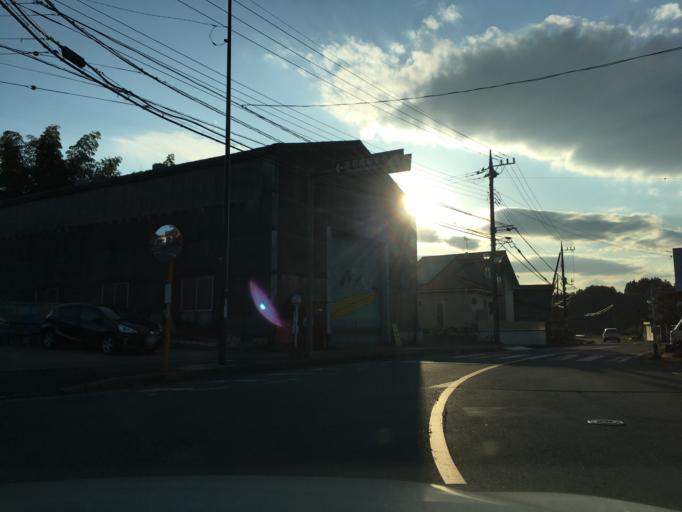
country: JP
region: Tochigi
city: Otawara
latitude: 36.8708
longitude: 140.1329
